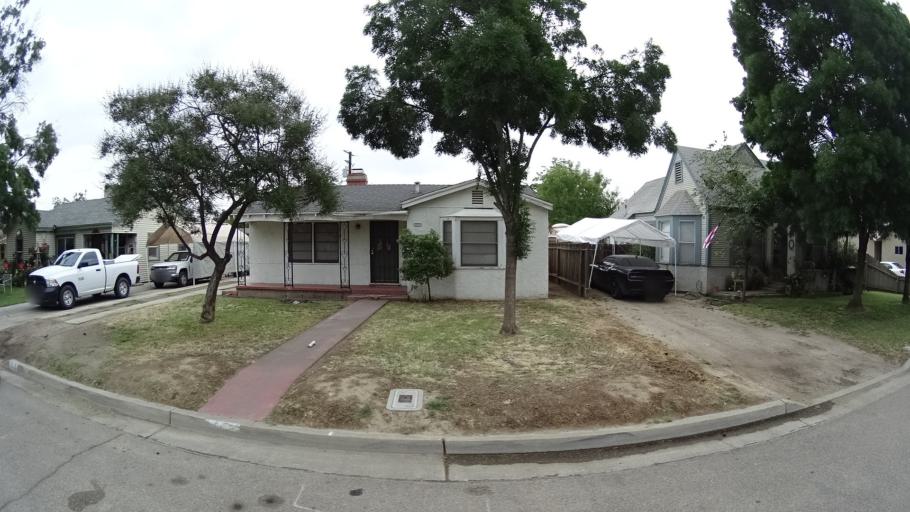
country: US
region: California
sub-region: Kings County
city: Hanford
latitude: 36.3414
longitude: -119.6409
